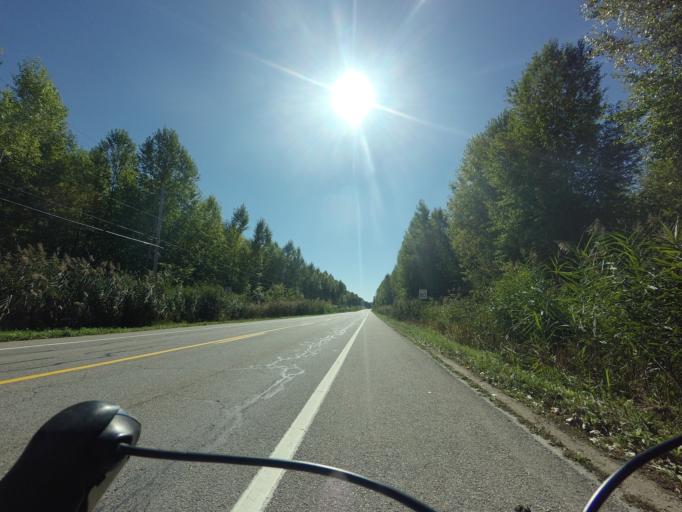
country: CA
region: Ontario
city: Clarence-Rockland
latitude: 45.5393
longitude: -75.4149
